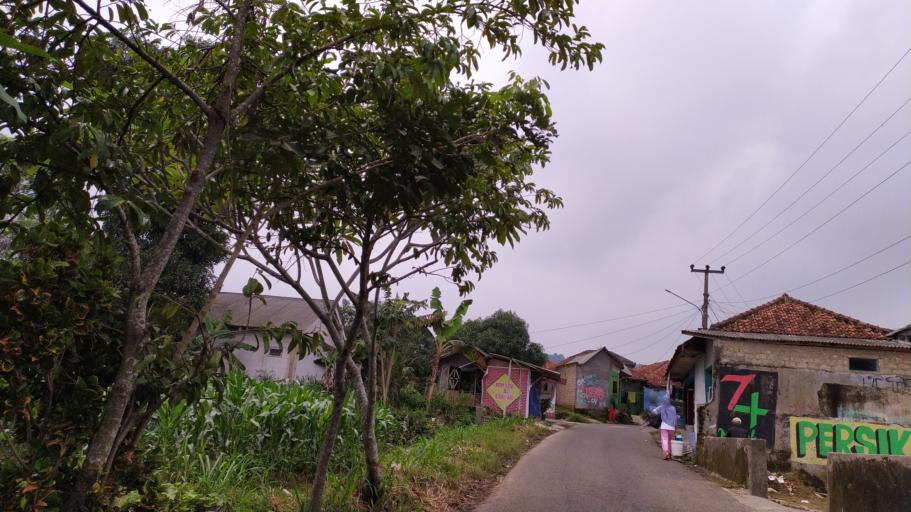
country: ID
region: West Java
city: Ciampea
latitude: -6.6149
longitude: 106.7091
